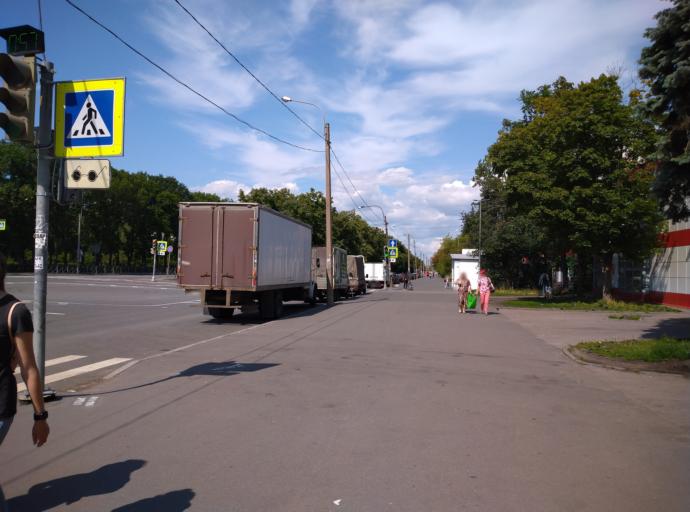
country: RU
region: St.-Petersburg
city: Kupchino
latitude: 59.8581
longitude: 30.3380
